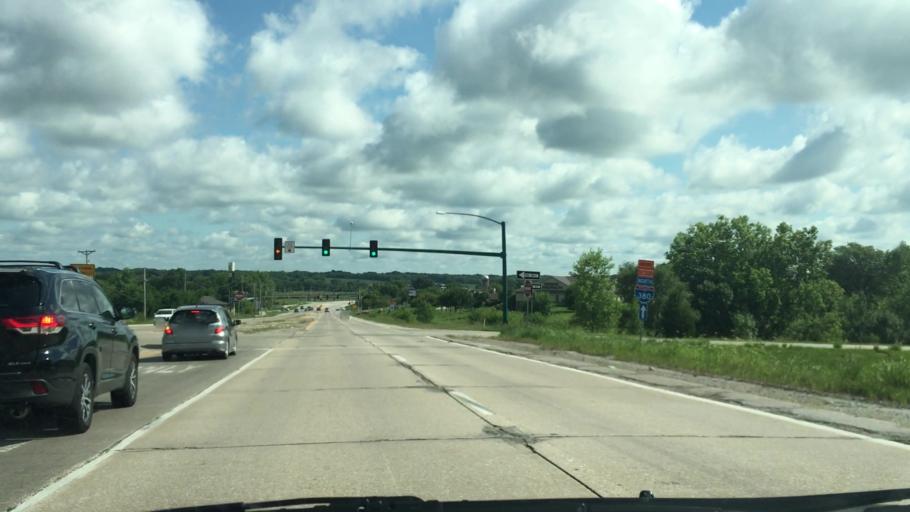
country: US
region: Iowa
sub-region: Johnson County
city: Iowa City
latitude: 41.6876
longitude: -91.4988
